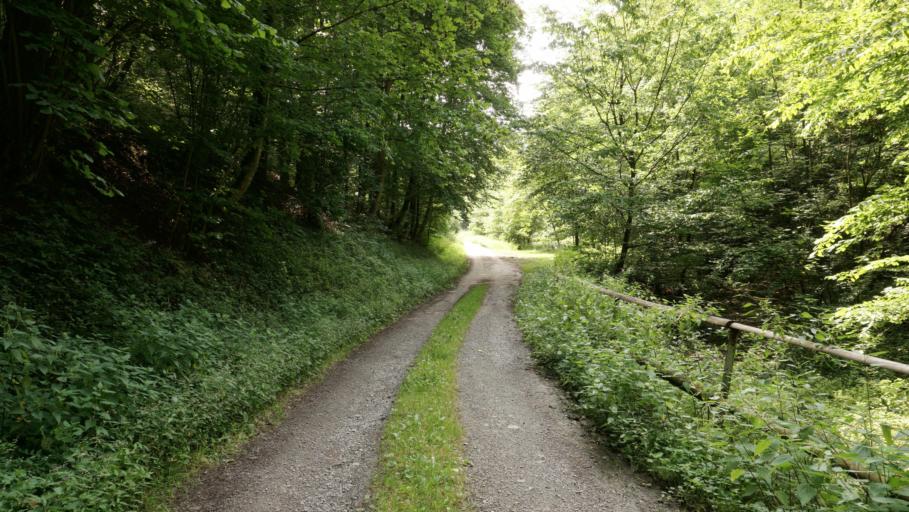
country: DE
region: Baden-Wuerttemberg
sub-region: Karlsruhe Region
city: Mosbach
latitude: 49.3346
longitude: 9.1529
